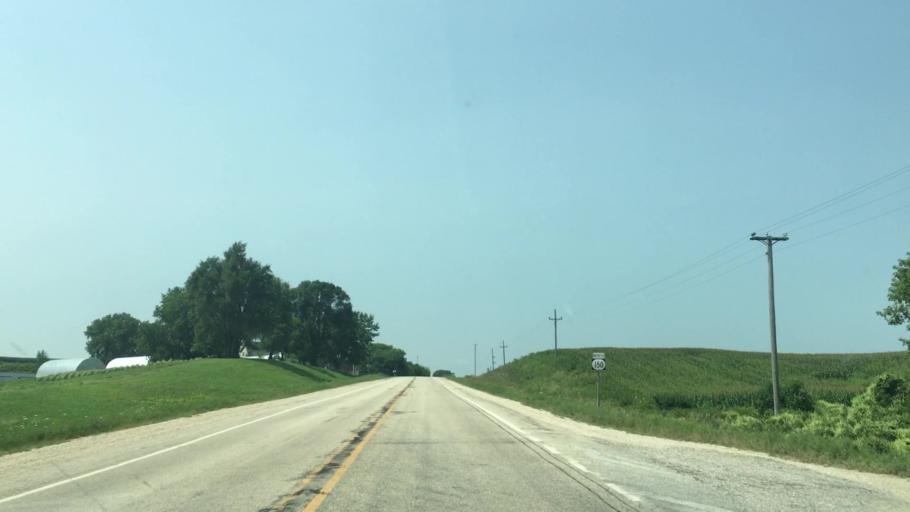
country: US
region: Iowa
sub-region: Fayette County
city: West Union
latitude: 43.0802
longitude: -91.8420
